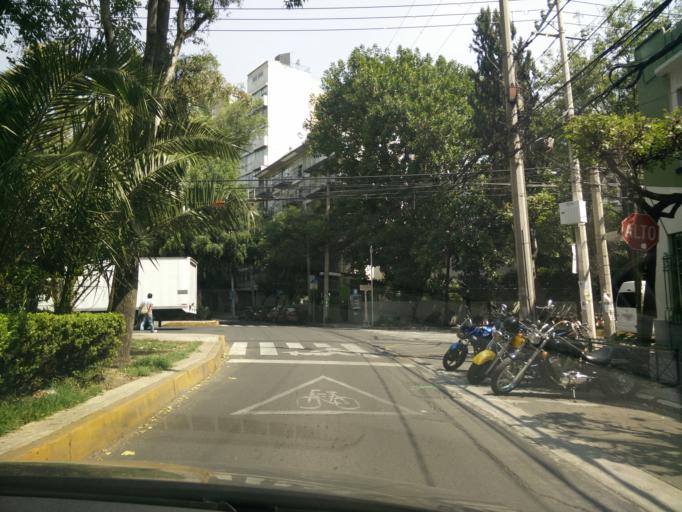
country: MX
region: Mexico City
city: Benito Juarez
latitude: 19.4150
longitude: -99.1667
